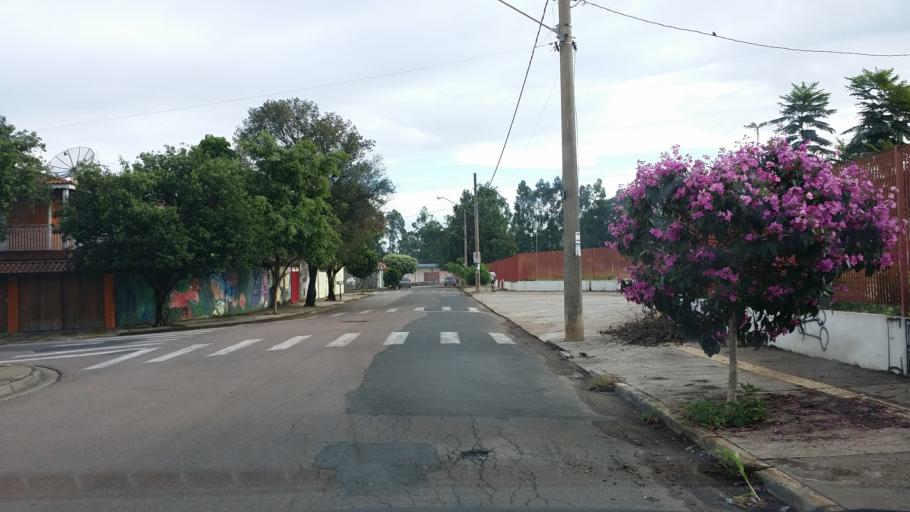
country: BR
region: Sao Paulo
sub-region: Indaiatuba
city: Indaiatuba
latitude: -23.1123
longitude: -47.2246
